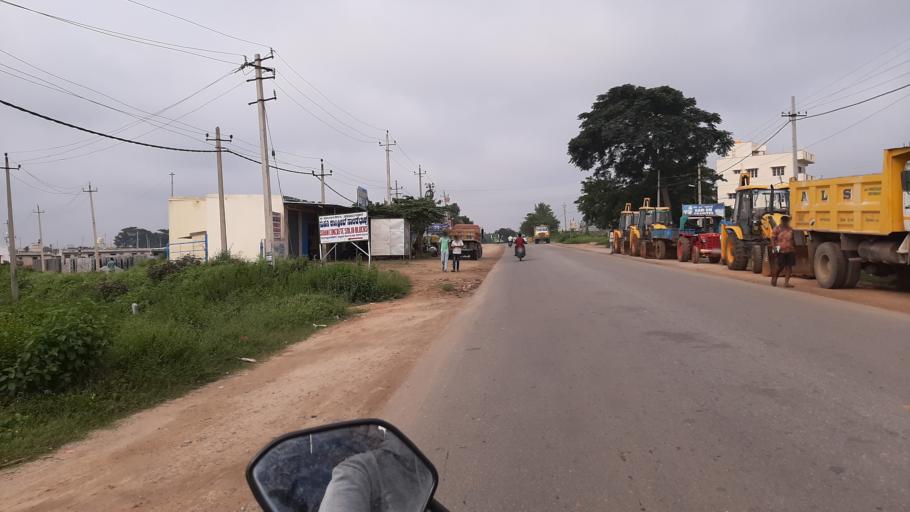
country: IN
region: Karnataka
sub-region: Bangalore Rural
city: Nelamangala
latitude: 12.9729
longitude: 77.4185
